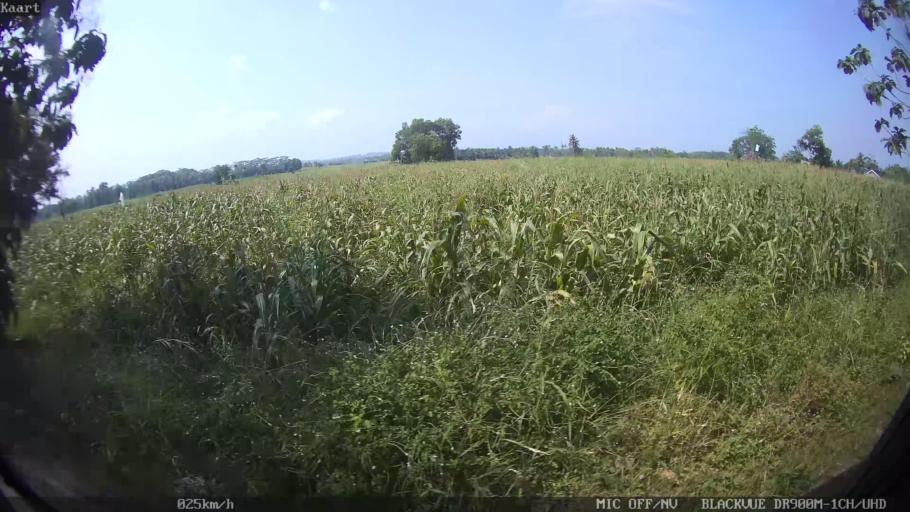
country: ID
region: Lampung
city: Natar
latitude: -5.2538
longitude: 105.2026
